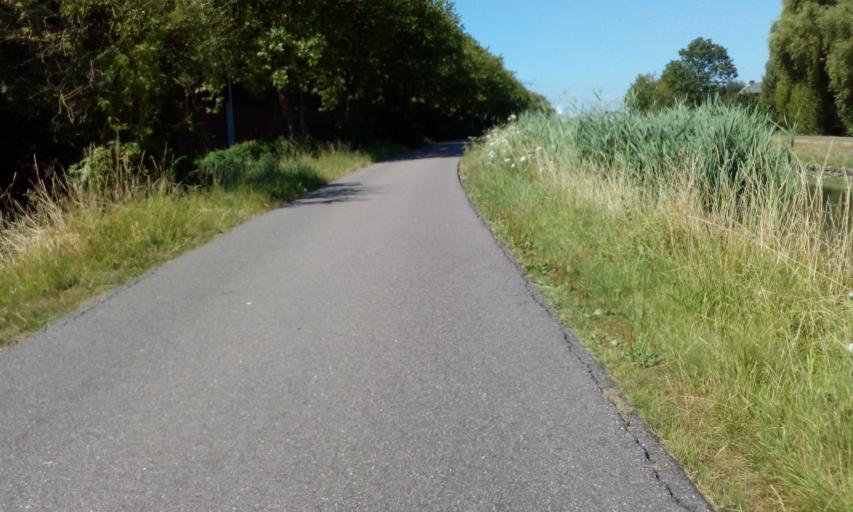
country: NL
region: South Holland
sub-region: Gemeente Westland
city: Naaldwijk
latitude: 51.9787
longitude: 4.2250
